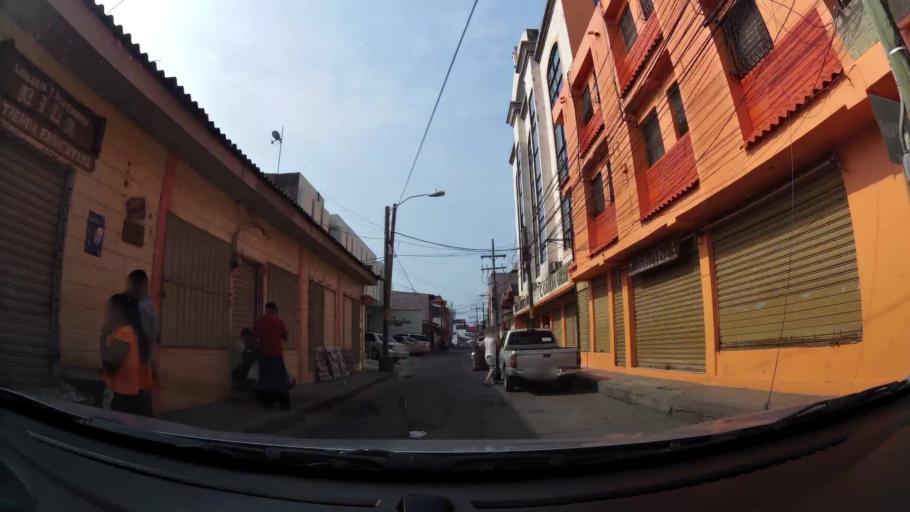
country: HN
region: Comayagua
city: Comayagua
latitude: 14.4571
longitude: -87.6415
